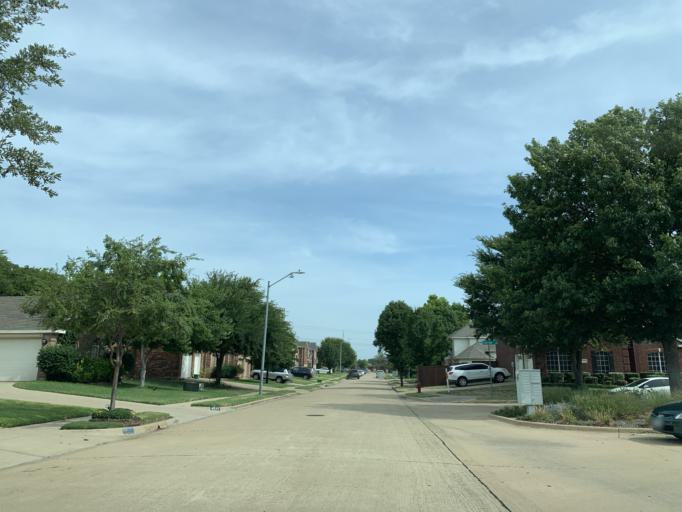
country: US
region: Texas
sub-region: Dallas County
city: Cedar Hill
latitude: 32.6587
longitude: -97.0064
